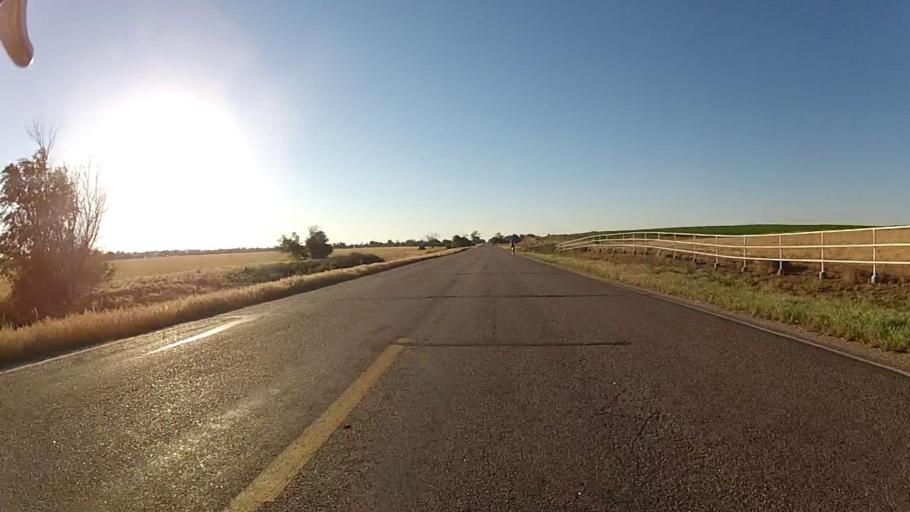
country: US
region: Kansas
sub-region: Ford County
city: Dodge City
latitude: 37.7185
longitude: -99.9440
